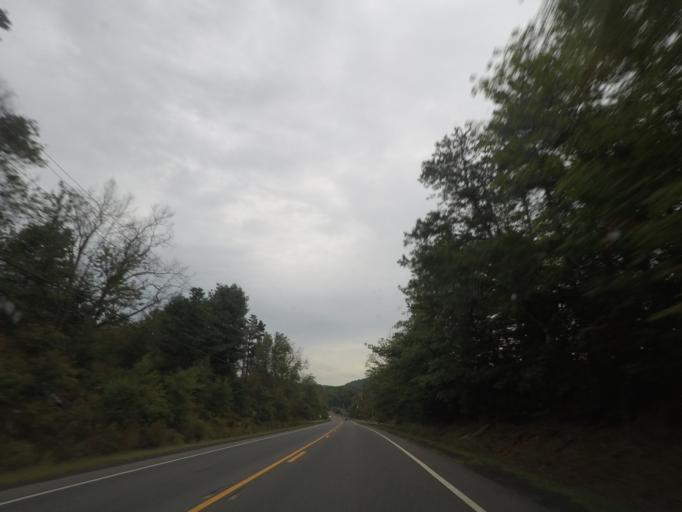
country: US
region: Massachusetts
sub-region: Hampshire County
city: Ware
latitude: 42.2096
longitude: -72.2510
